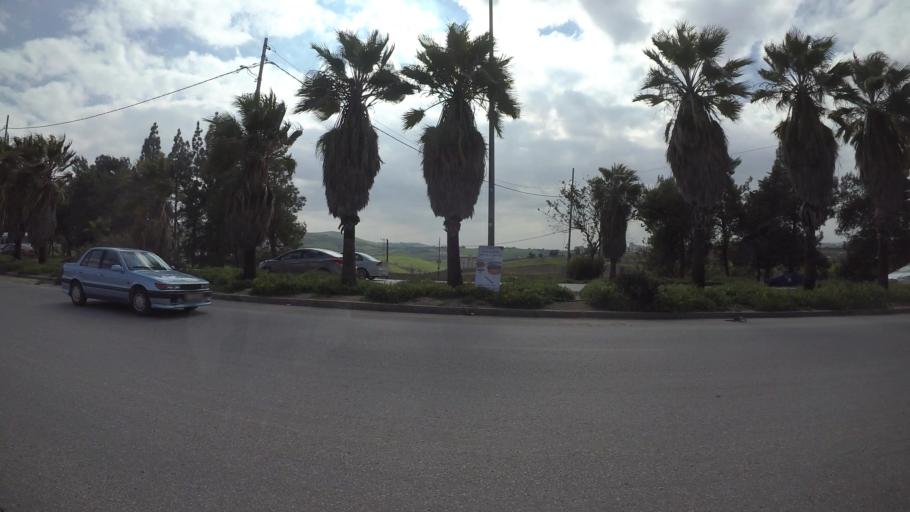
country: JO
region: Balqa
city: As Salt
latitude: 32.0391
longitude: 35.7886
